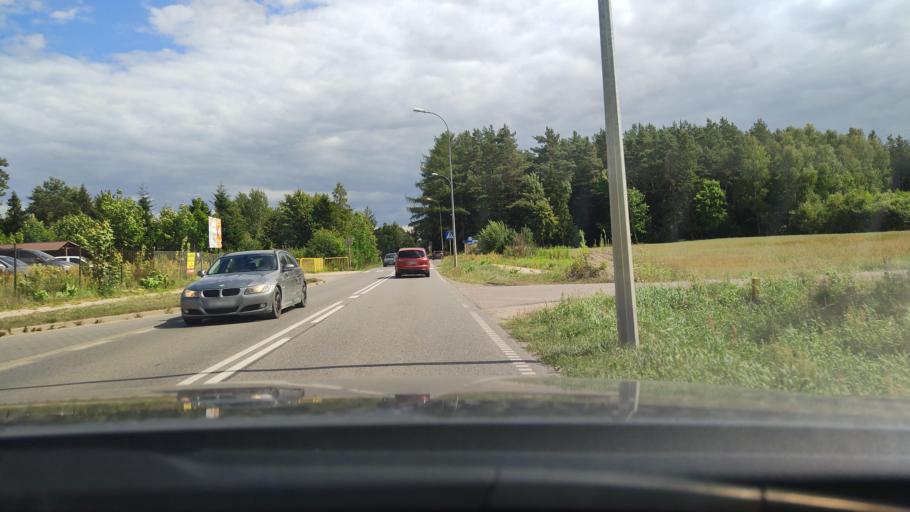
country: PL
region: Pomeranian Voivodeship
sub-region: Powiat wejherowski
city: Koleczkowo
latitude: 54.4801
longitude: 18.3577
